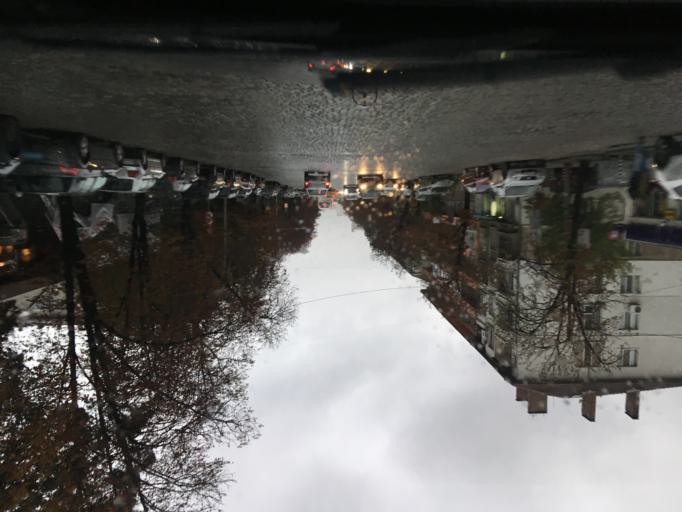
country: BG
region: Sofia-Capital
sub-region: Stolichna Obshtina
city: Sofia
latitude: 42.6891
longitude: 23.3078
